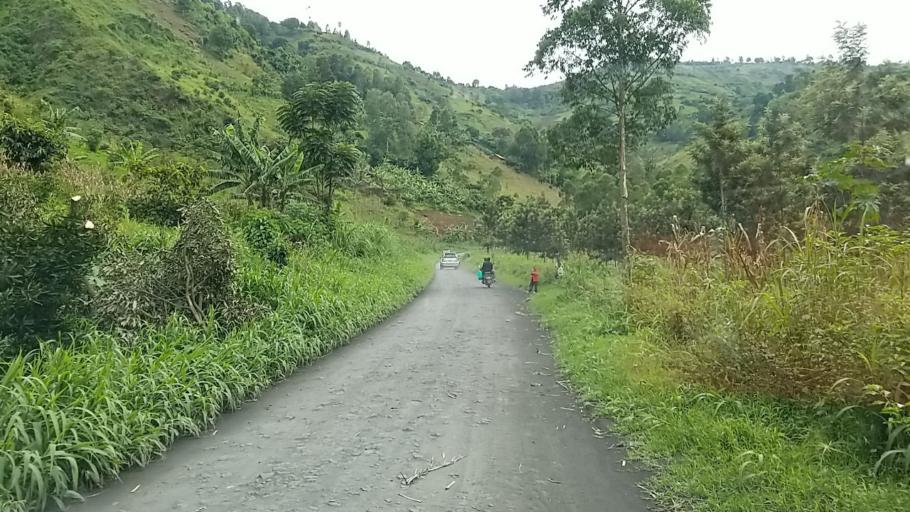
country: CD
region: Nord Kivu
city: Sake
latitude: -1.7347
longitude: 29.0069
